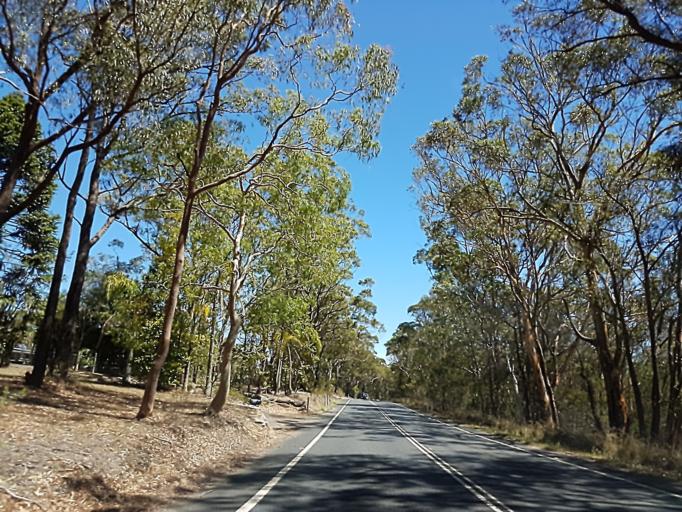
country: AU
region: New South Wales
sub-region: Hornsby Shire
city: Glenorie
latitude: -33.5077
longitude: 151.0240
